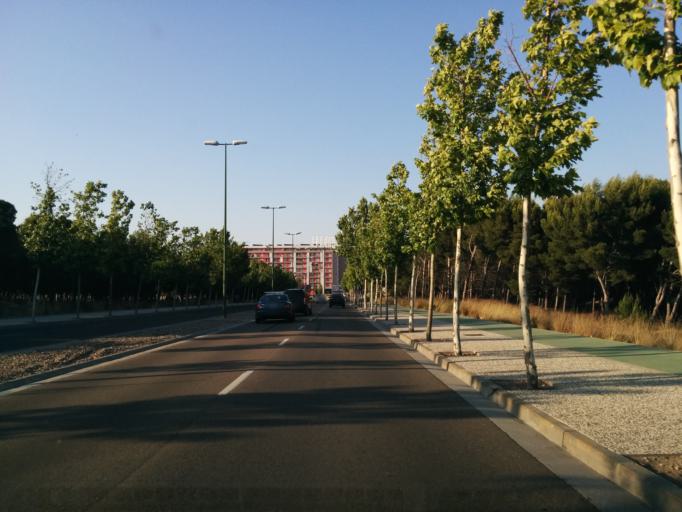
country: ES
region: Aragon
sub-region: Provincia de Zaragoza
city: Zaragoza
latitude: 41.6122
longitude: -0.8763
